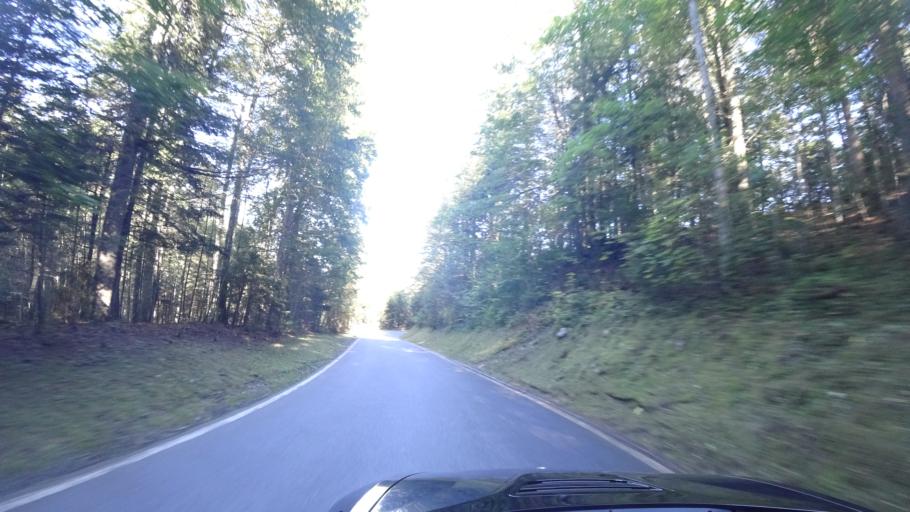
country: CH
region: Obwalden
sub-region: Obwalden
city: Giswil
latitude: 46.8302
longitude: 8.1247
